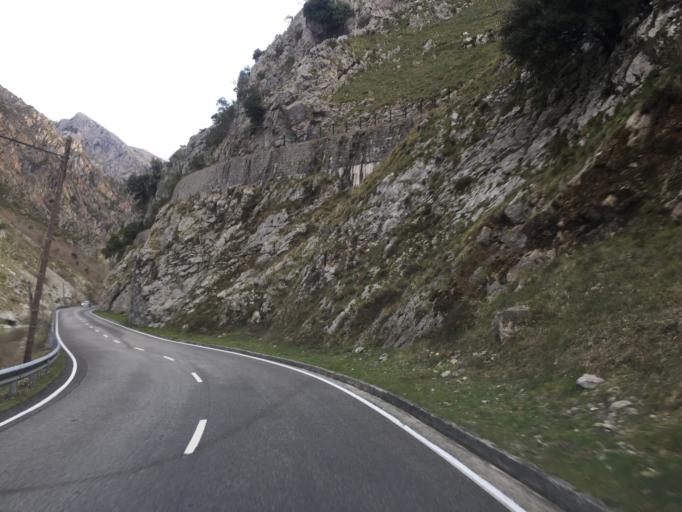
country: ES
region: Asturias
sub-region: Province of Asturias
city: Carrena
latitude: 43.2699
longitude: -4.8310
